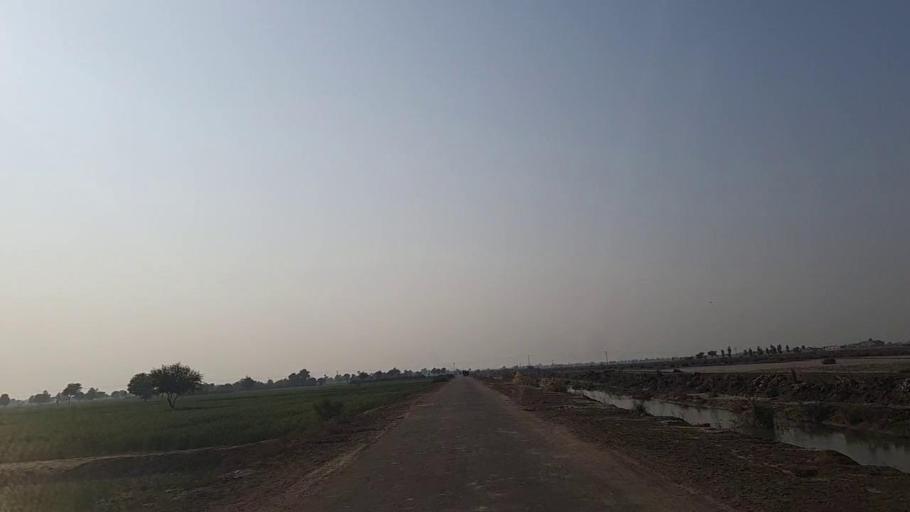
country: PK
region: Sindh
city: Jam Sahib
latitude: 26.2855
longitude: 68.6166
